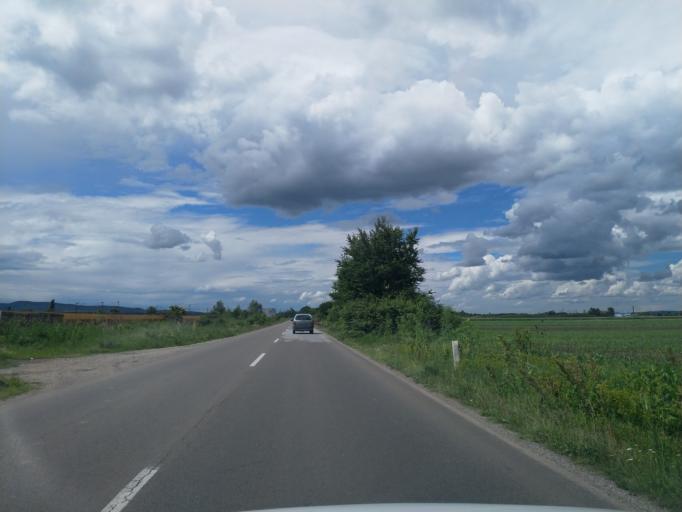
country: RS
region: Central Serbia
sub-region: Pomoravski Okrug
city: Paracin
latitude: 43.8823
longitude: 21.3876
